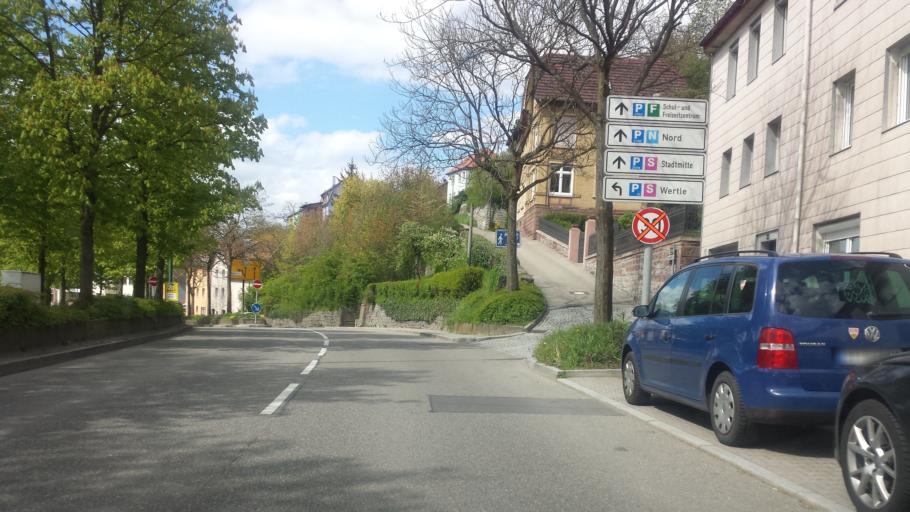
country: DE
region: Baden-Wuerttemberg
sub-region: Karlsruhe Region
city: Muhlacker
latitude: 48.9439
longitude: 8.8443
